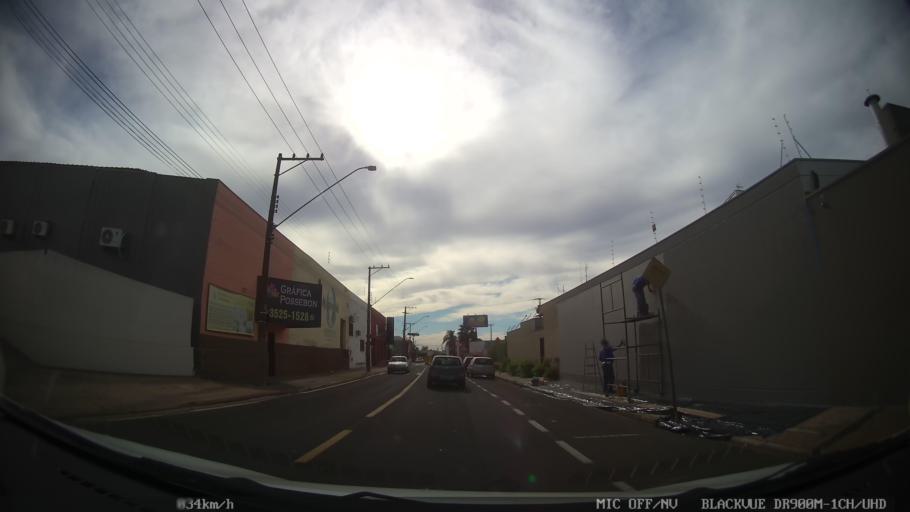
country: BR
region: Sao Paulo
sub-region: Catanduva
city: Catanduva
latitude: -21.1422
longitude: -48.9824
